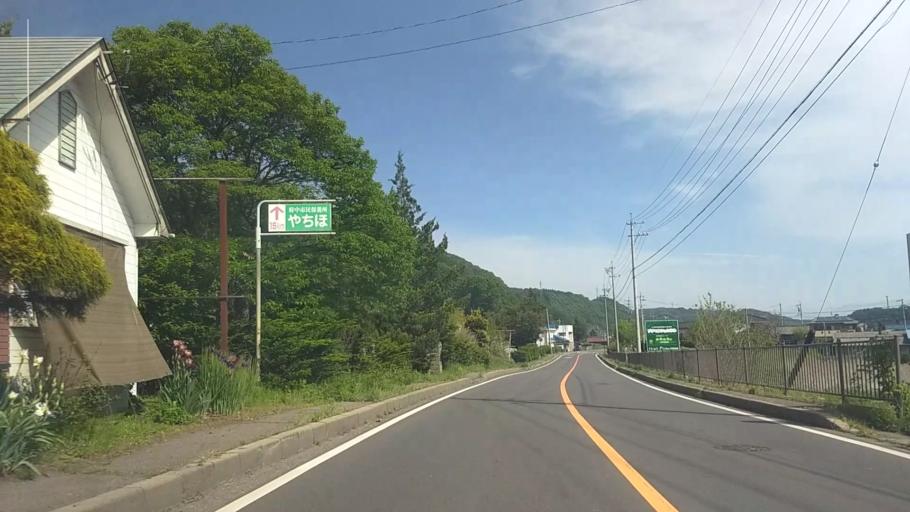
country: JP
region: Nagano
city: Saku
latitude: 36.1118
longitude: 138.4746
